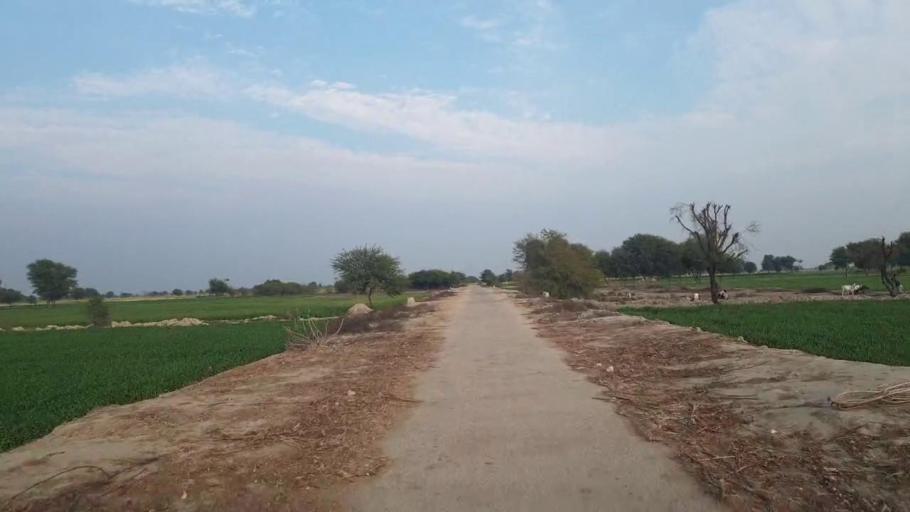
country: PK
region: Sindh
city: Shahpur Chakar
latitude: 26.0978
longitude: 68.5449
